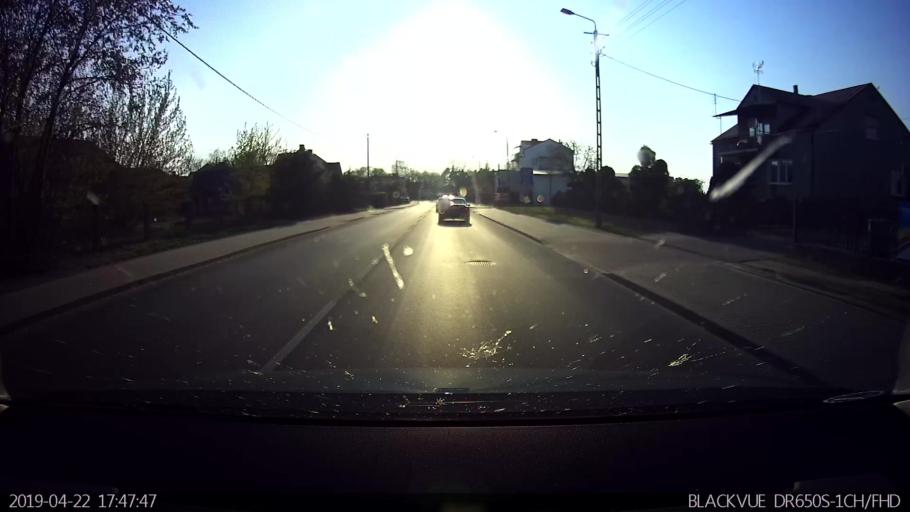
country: PL
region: Masovian Voivodeship
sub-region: Powiat wegrowski
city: Wegrow
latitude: 52.4040
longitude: 22.0180
